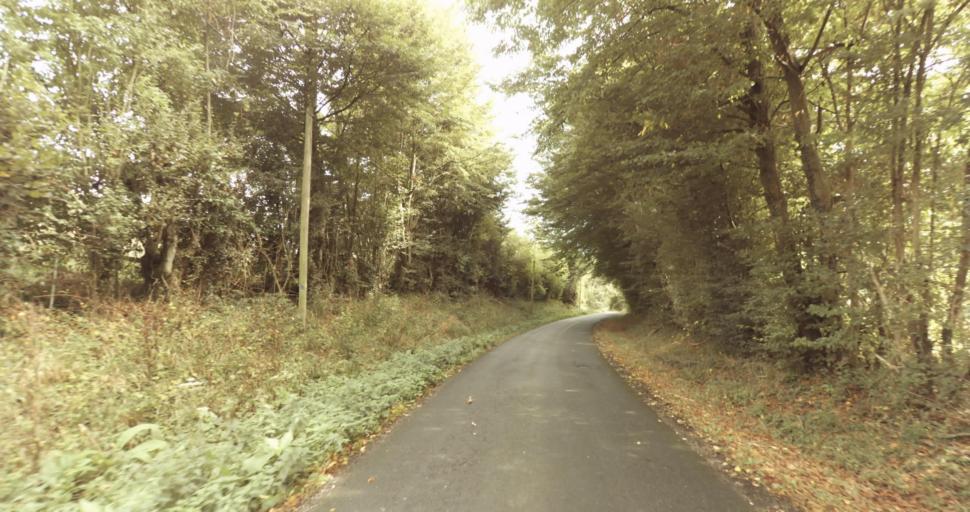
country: FR
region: Lower Normandy
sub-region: Departement de l'Orne
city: Vimoutiers
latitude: 48.8571
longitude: 0.2043
